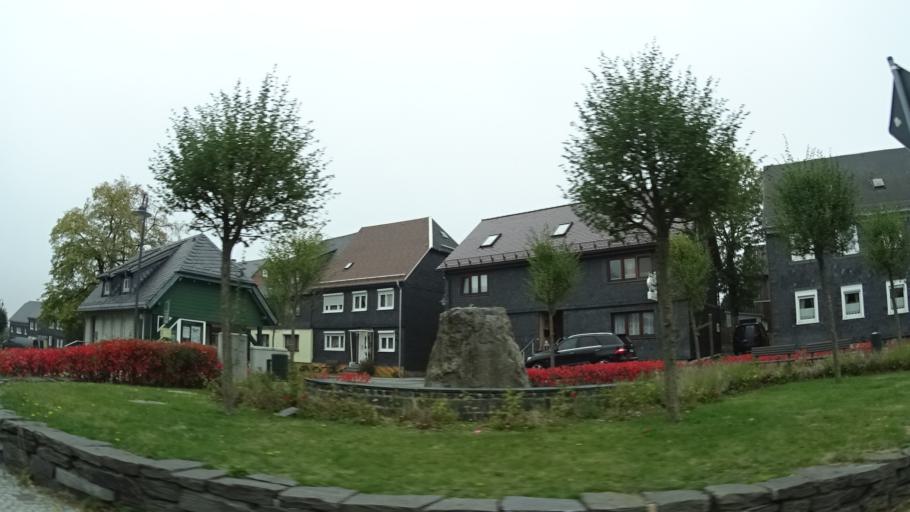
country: DE
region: Thuringia
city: Herschdorf
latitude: 50.6288
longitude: 11.0507
